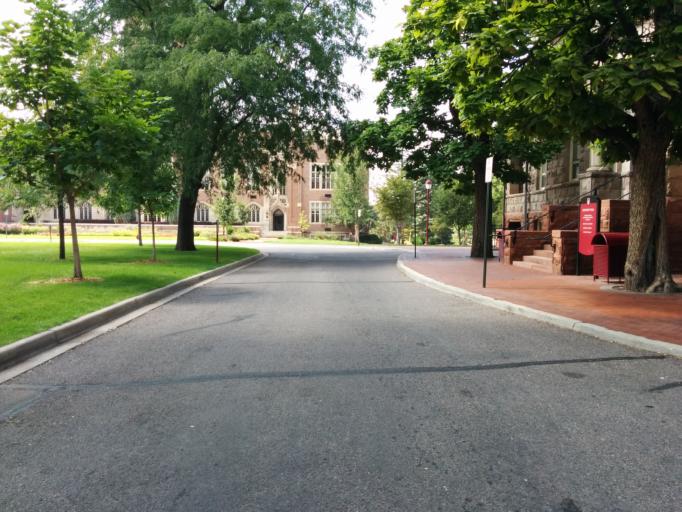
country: US
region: Colorado
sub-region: Arapahoe County
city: Cherry Hills Village
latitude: 39.6768
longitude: -104.9604
